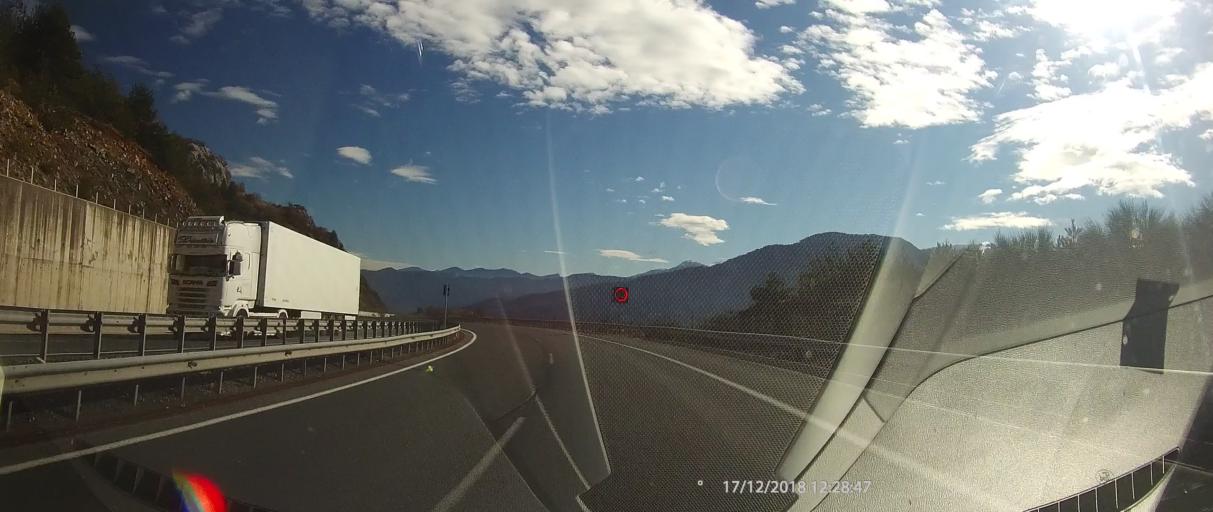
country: GR
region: Epirus
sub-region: Nomos Ioanninon
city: Metsovo
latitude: 39.7878
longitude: 21.2802
